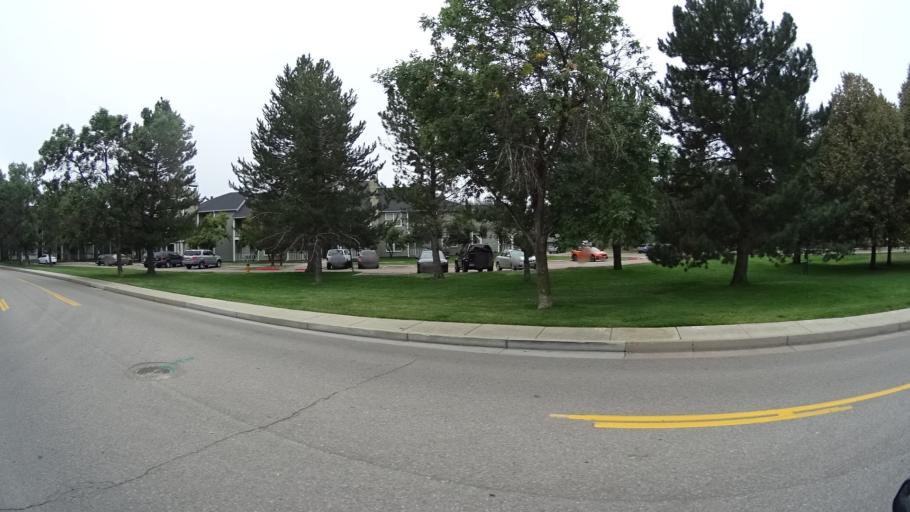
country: US
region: Colorado
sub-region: El Paso County
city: Cimarron Hills
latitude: 38.9309
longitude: -104.7719
